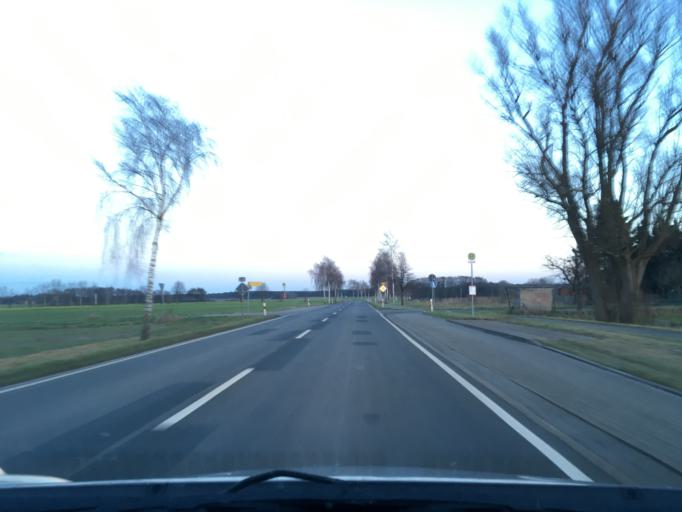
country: DE
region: Lower Saxony
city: Waddeweitz
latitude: 52.9869
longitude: 10.9865
